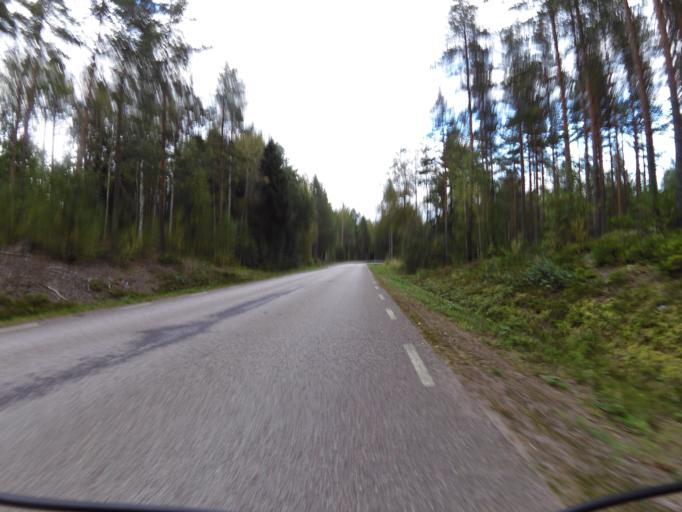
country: SE
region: Gaevleborg
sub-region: Sandvikens Kommun
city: Sandviken
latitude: 60.6571
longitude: 16.8421
